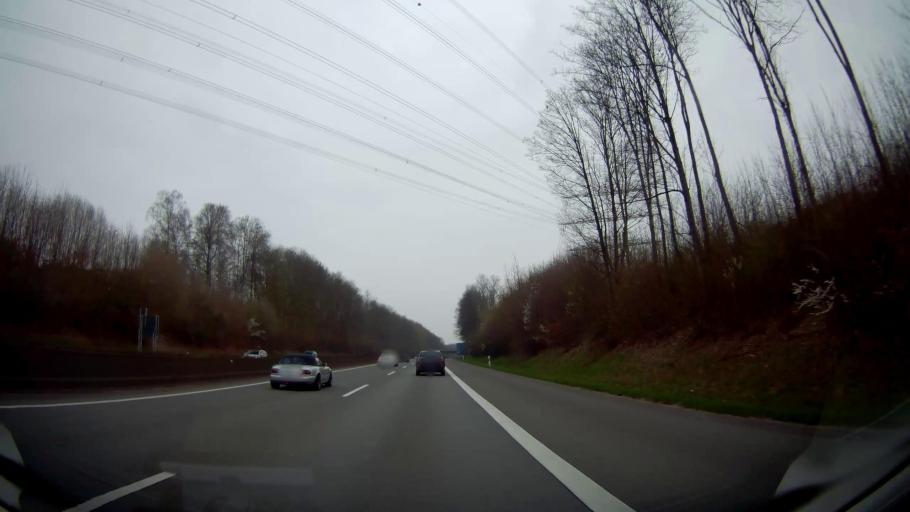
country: DE
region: North Rhine-Westphalia
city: Castrop-Rauxel
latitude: 51.5430
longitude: 7.3624
